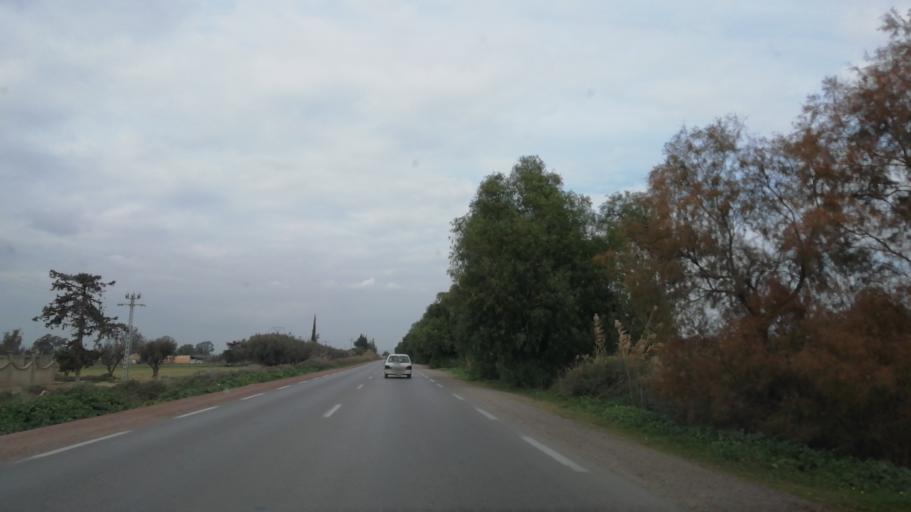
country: DZ
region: Mostaganem
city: Mostaganem
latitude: 35.6592
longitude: 0.0588
